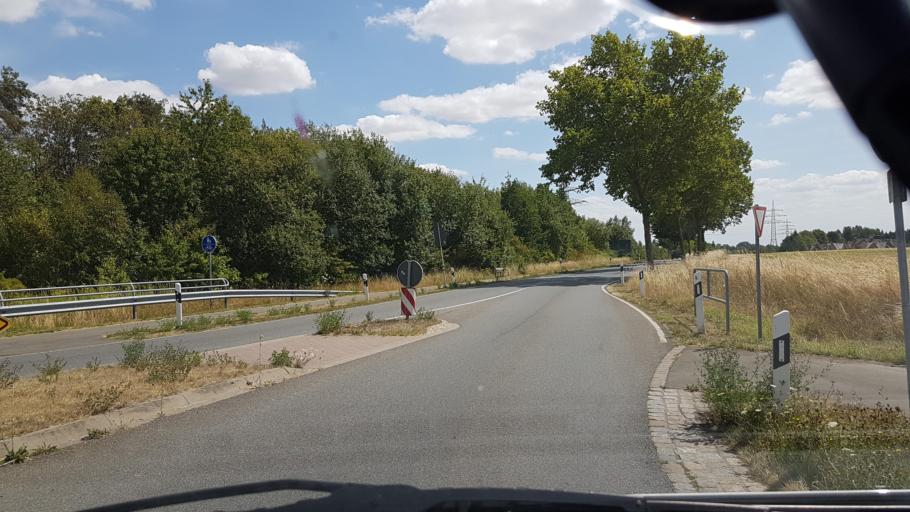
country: DE
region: Lower Saxony
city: Schoningen
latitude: 52.1496
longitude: 10.9730
